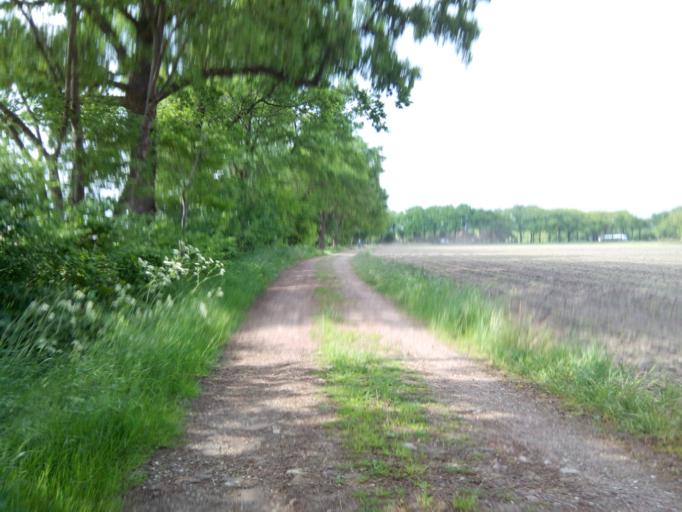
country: NL
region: Gelderland
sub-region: Berkelland
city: Borculo
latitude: 52.0997
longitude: 6.4968
